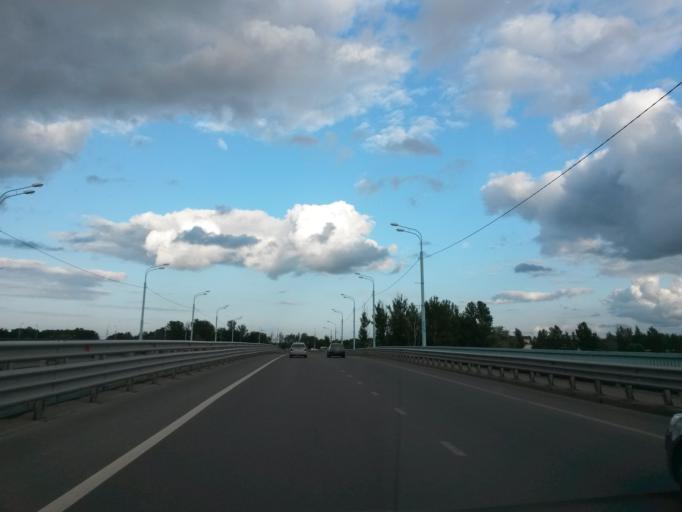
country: RU
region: Jaroslavl
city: Yaroslavl
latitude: 57.6196
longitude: 39.8807
